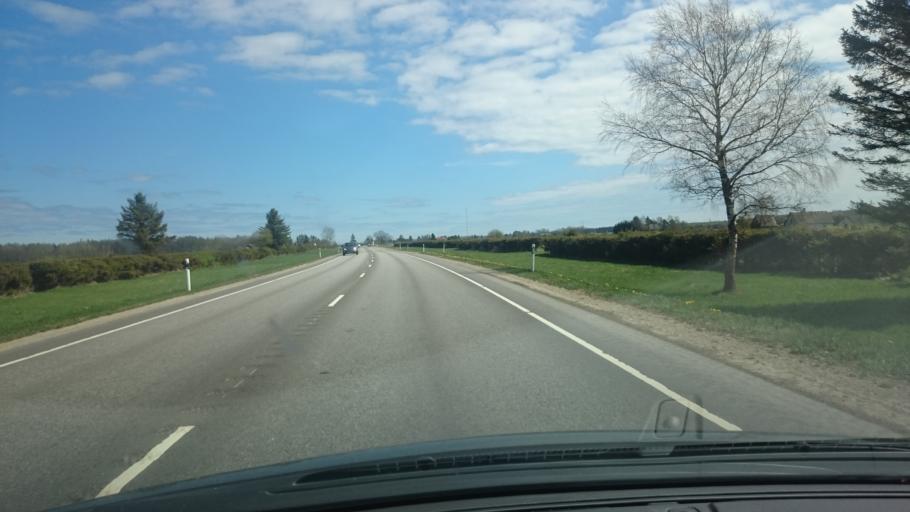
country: EE
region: Ida-Virumaa
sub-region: Kohtla-Nomme vald
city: Kohtla-Nomme
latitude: 59.4187
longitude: 27.1631
